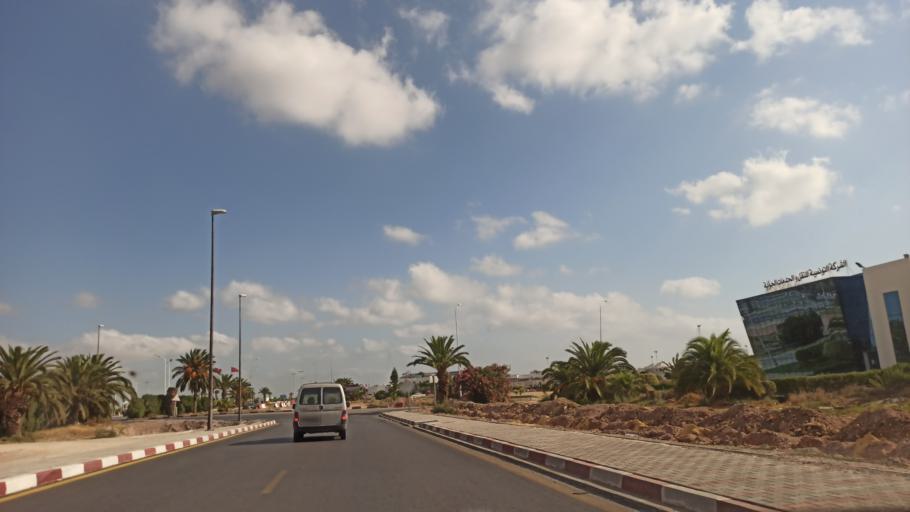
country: TN
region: Ariana
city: Ariana
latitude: 36.8423
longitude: 10.2152
